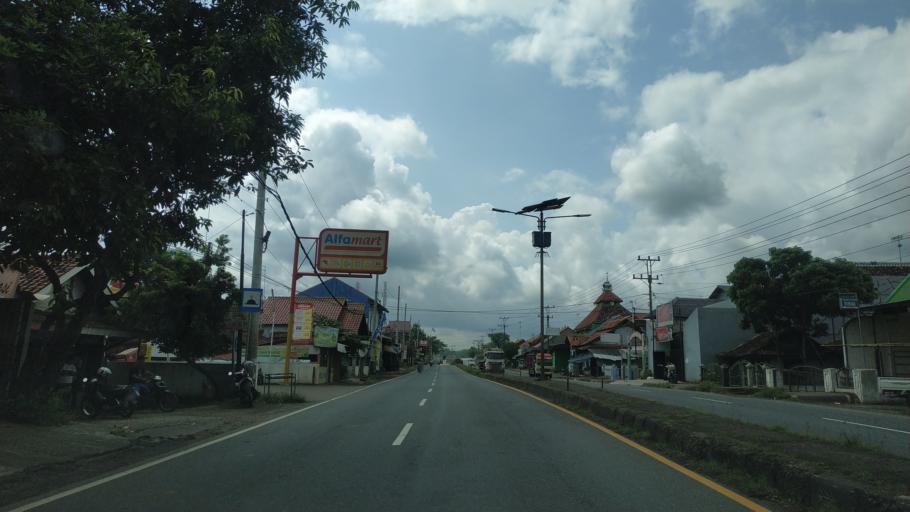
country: ID
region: Central Java
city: Pekalongan
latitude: -6.9519
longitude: 109.8025
